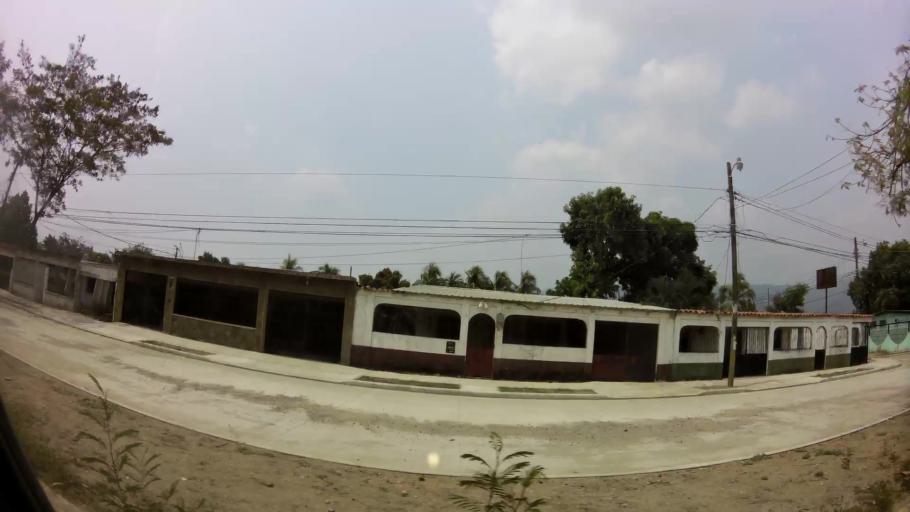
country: HN
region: Cortes
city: San Pedro Sula
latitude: 15.4818
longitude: -88.0198
